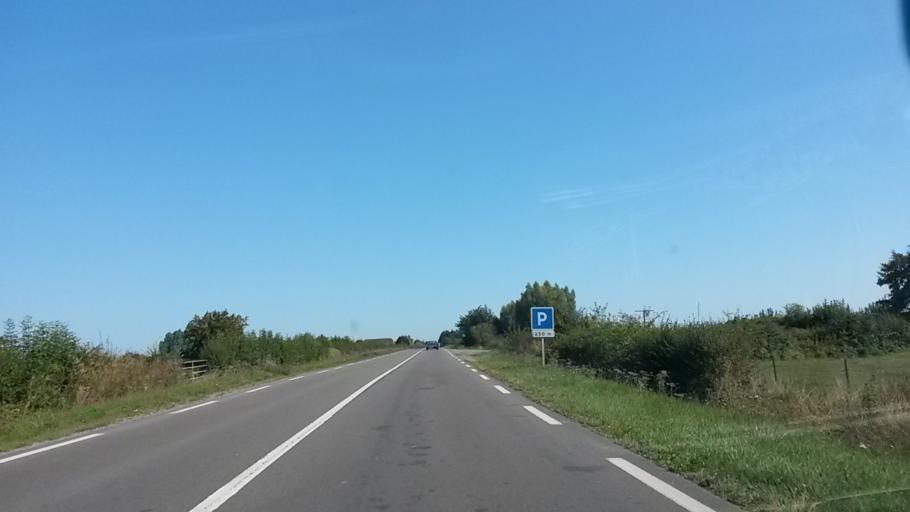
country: FR
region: Nord-Pas-de-Calais
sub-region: Departement du Nord
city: Avesnelles
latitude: 50.1451
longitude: 3.9483
